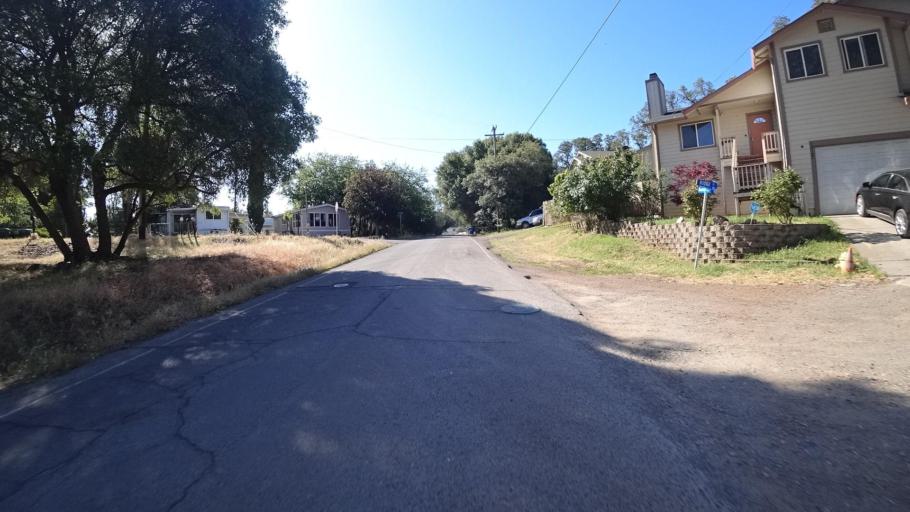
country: US
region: California
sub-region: Lake County
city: Clearlake
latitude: 38.9745
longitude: -122.6663
